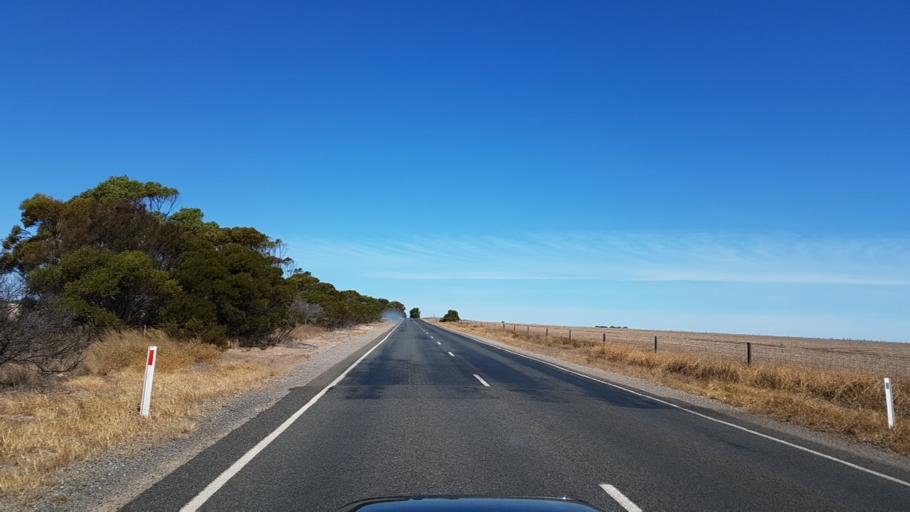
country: AU
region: South Australia
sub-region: Yorke Peninsula
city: Maitland
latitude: -34.3434
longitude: 137.6591
